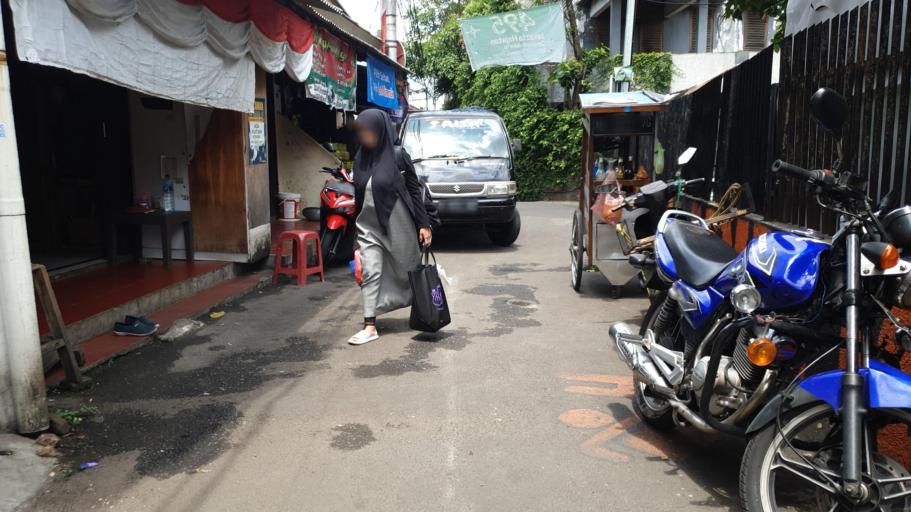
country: ID
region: Banten
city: South Tangerang
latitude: -6.2663
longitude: 106.7896
